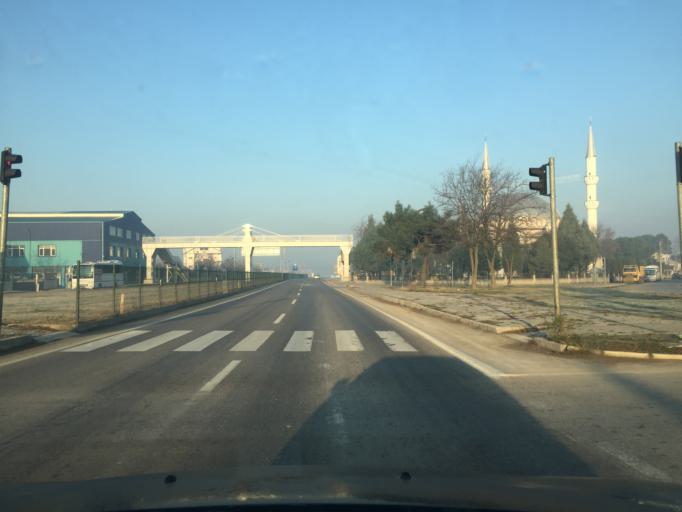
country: TR
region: Sakarya
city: Akyazi
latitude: 40.6344
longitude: 30.6283
